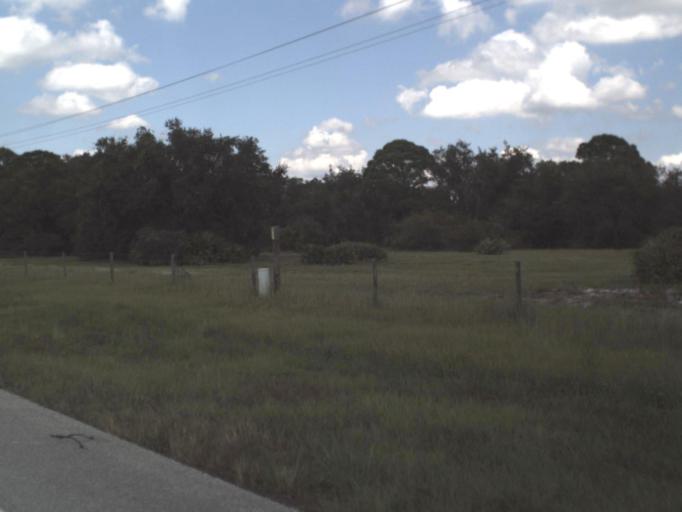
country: US
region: Florida
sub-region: Okeechobee County
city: Okeechobee
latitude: 27.3658
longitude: -81.0664
